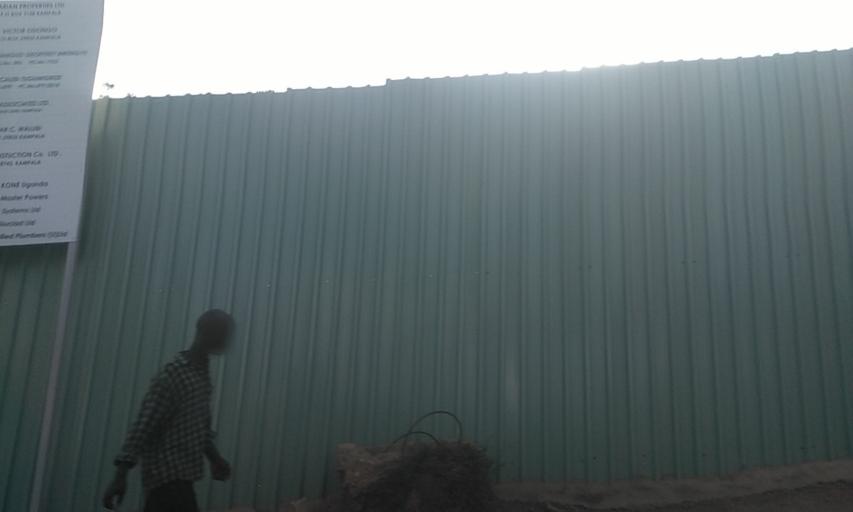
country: UG
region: Central Region
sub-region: Kampala District
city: Kampala
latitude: 0.3364
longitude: 32.6004
